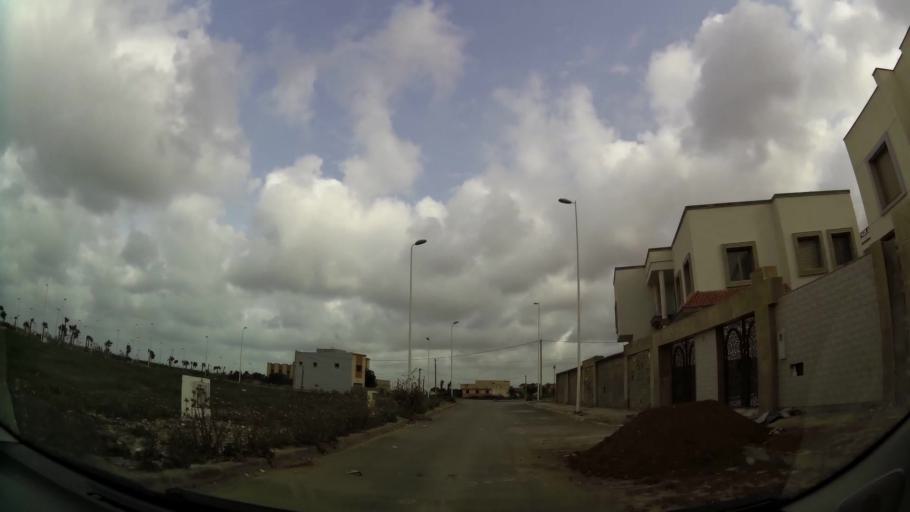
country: MA
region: Oriental
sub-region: Nador
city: Nador
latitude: 35.1647
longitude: -2.9125
